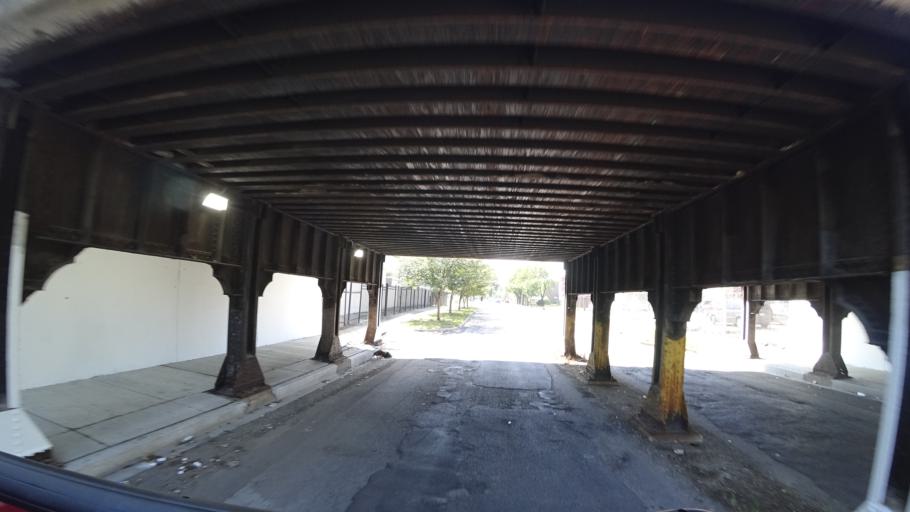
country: US
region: Illinois
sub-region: Cook County
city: Cicero
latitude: 41.8685
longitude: -87.7301
